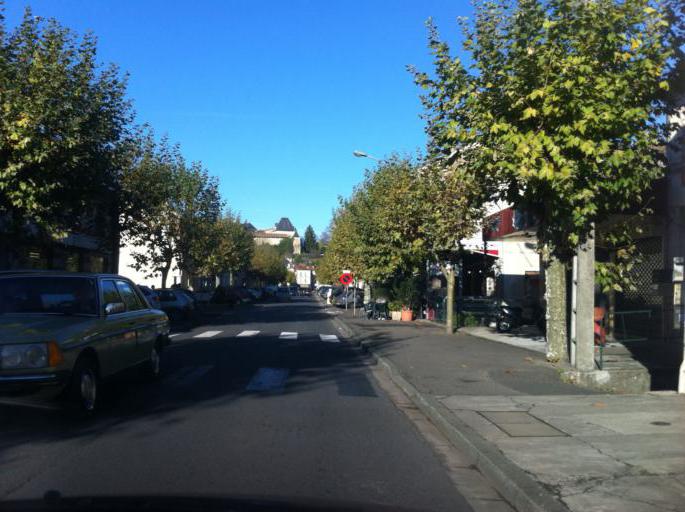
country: FR
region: Aquitaine
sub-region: Departement de la Dordogne
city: Saint-Aulaye
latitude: 45.2689
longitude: 0.1687
